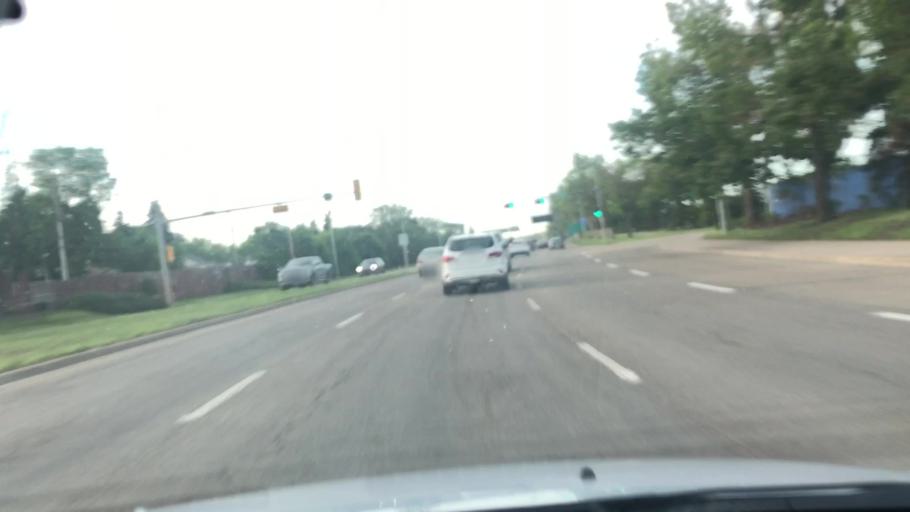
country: CA
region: Alberta
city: Edmonton
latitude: 53.5688
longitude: -113.4519
